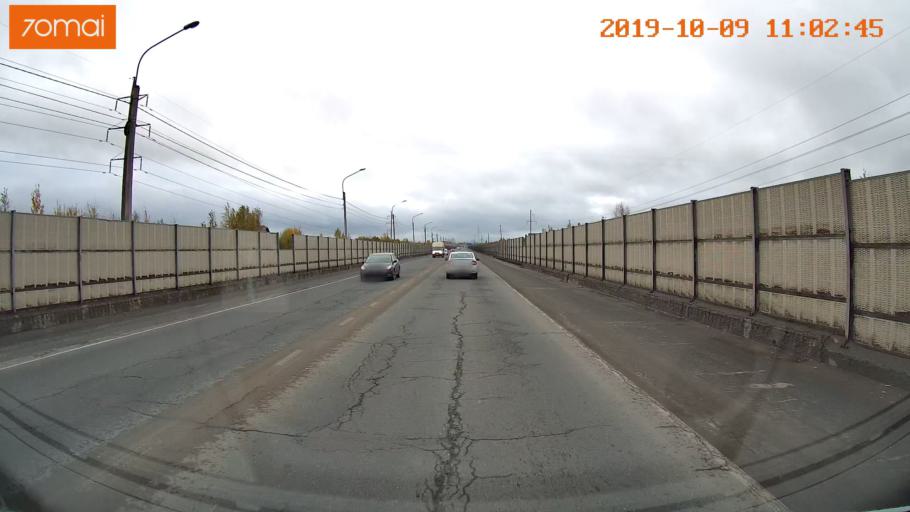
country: RU
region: Vologda
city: Vologda
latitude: 59.2287
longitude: 39.7748
